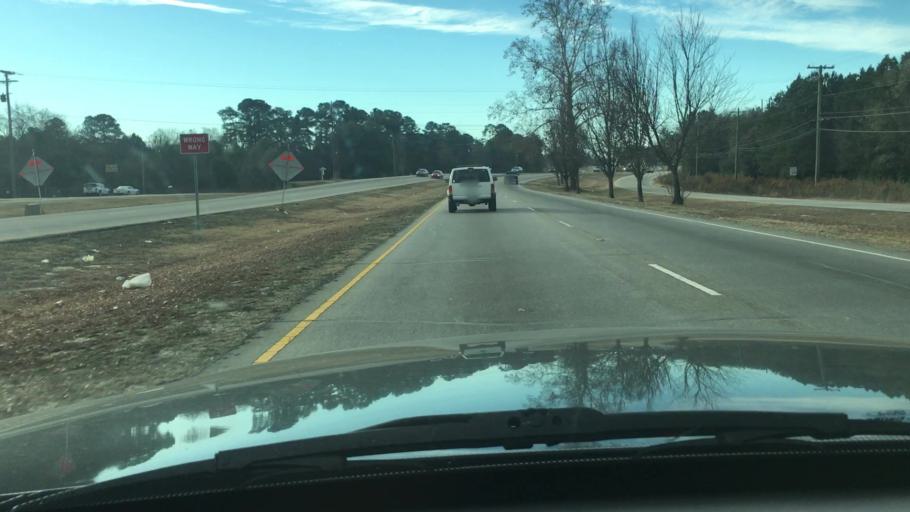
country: US
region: North Carolina
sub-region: Cumberland County
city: Fayetteville
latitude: 35.0108
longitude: -78.8975
